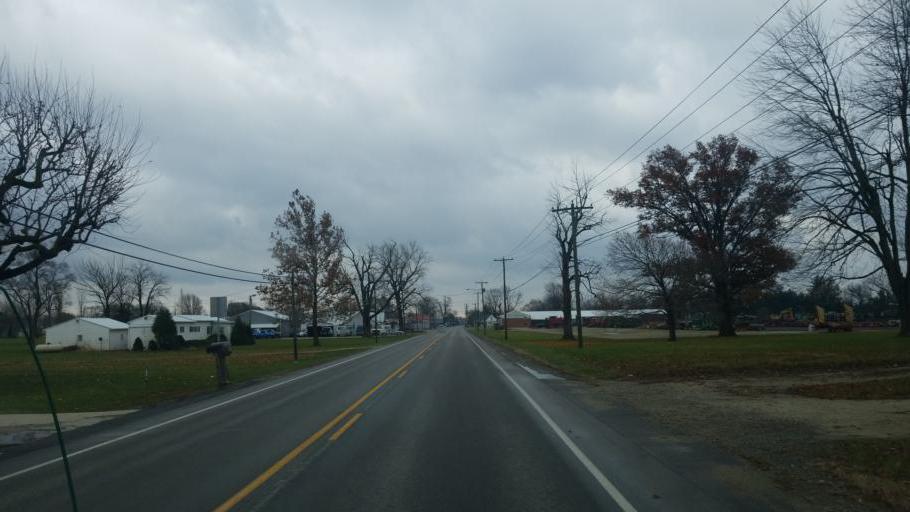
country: US
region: Indiana
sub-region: Adams County
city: Geneva
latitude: 40.5391
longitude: -84.9647
